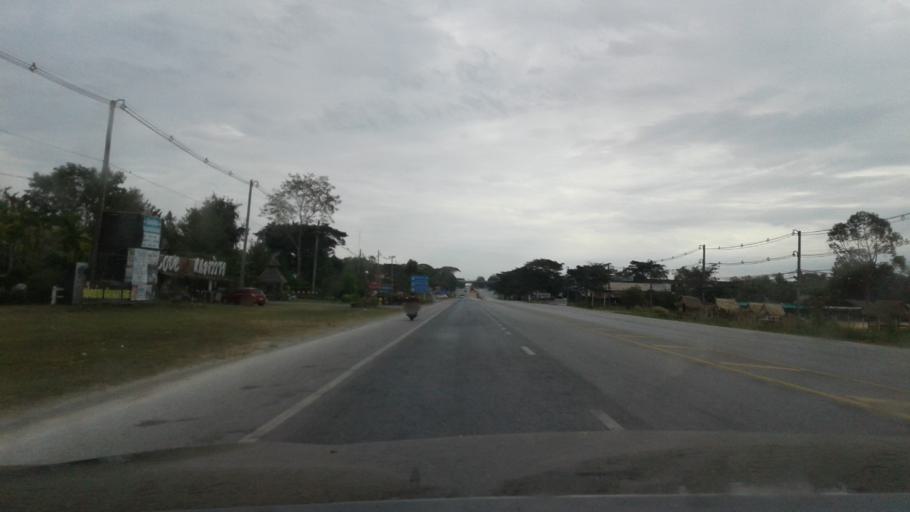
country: TH
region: Changwat Udon Thani
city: Nong Wua So
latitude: 17.2666
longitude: 102.5935
